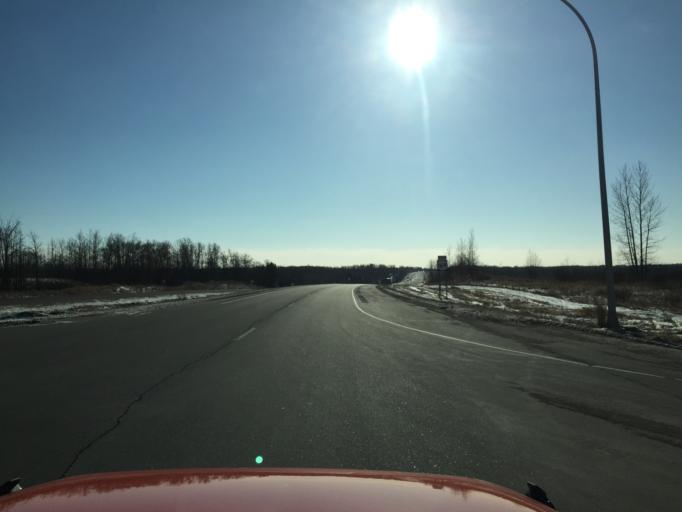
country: US
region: Minnesota
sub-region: Mille Lacs County
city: Milaca
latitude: 45.8223
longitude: -93.6559
